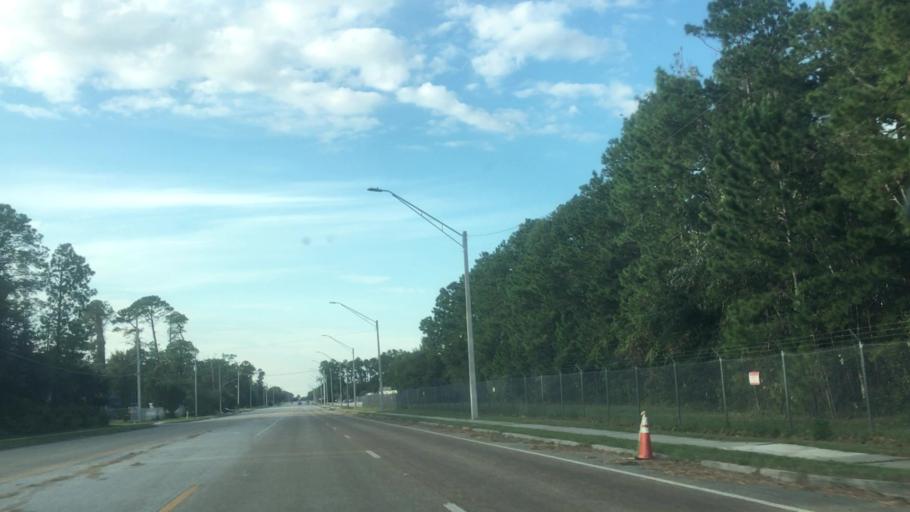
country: US
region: Florida
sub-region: Duval County
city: Atlantic Beach
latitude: 30.3280
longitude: -81.5231
